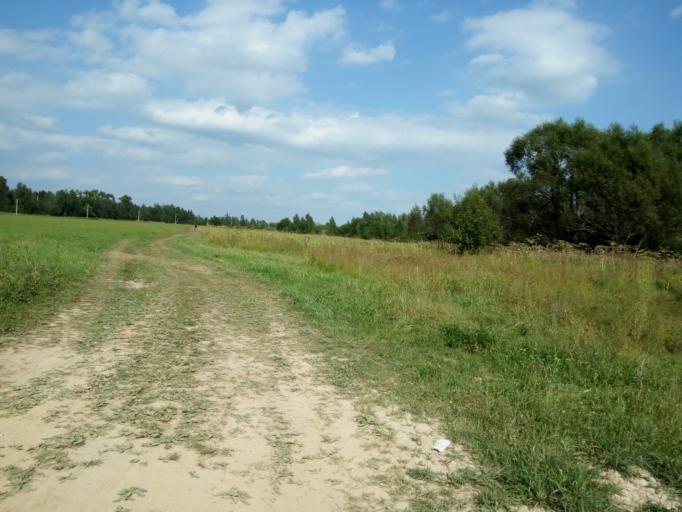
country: RU
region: Moskovskaya
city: Kubinka
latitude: 55.5848
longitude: 36.7372
